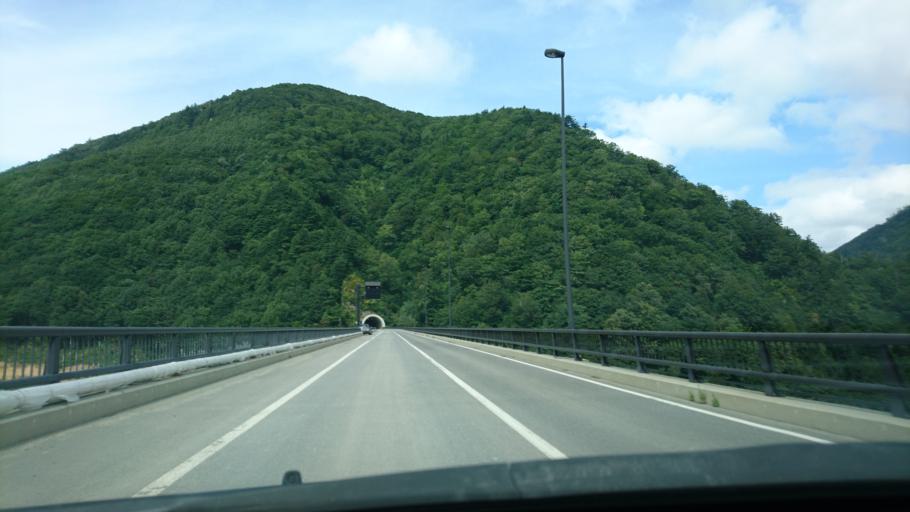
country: JP
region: Akita
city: Yuzawa
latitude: 39.0369
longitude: 140.7350
